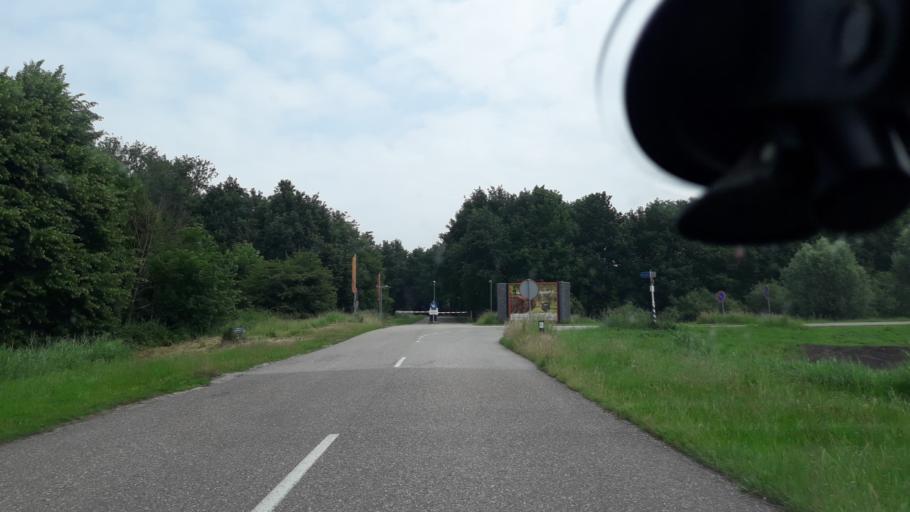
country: NL
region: Flevoland
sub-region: Gemeente Lelystad
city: Lelystad
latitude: 52.4808
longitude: 5.5273
